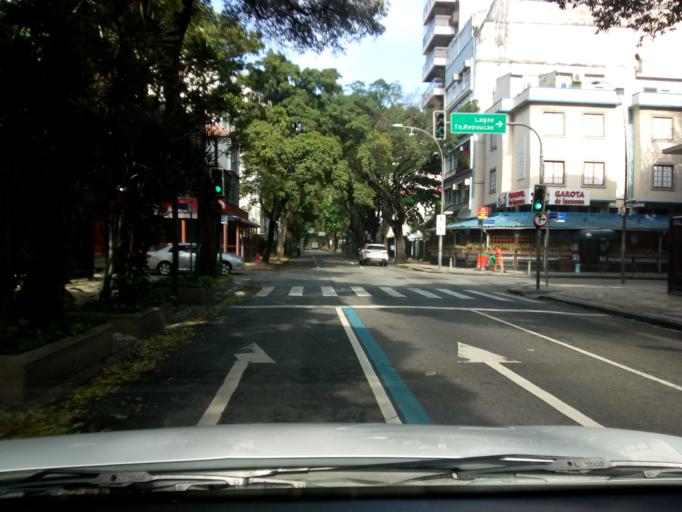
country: BR
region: Rio de Janeiro
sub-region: Rio De Janeiro
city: Rio de Janeiro
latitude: -22.9854
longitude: -43.2024
